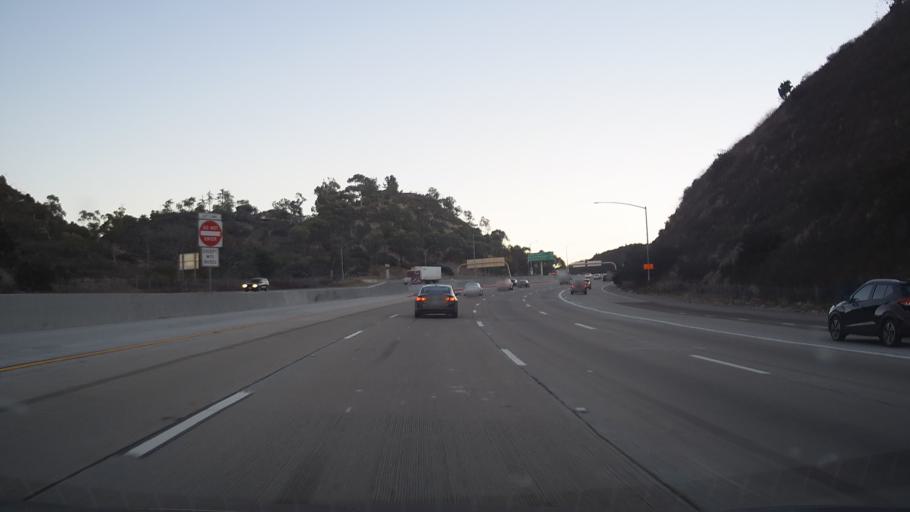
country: US
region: California
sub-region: San Diego County
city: San Diego
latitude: 32.7765
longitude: -117.1128
